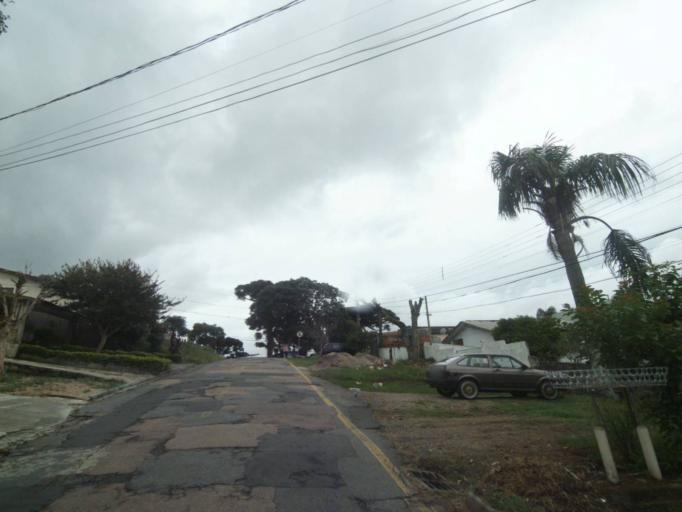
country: BR
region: Parana
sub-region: Curitiba
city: Curitiba
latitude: -25.4560
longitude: -49.3249
